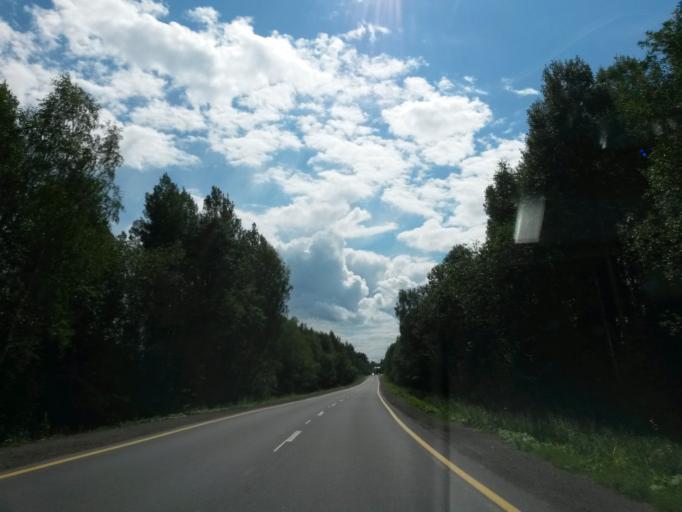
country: RU
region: Jaroslavl
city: Gavrilov-Yam
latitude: 57.2877
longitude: 39.9528
